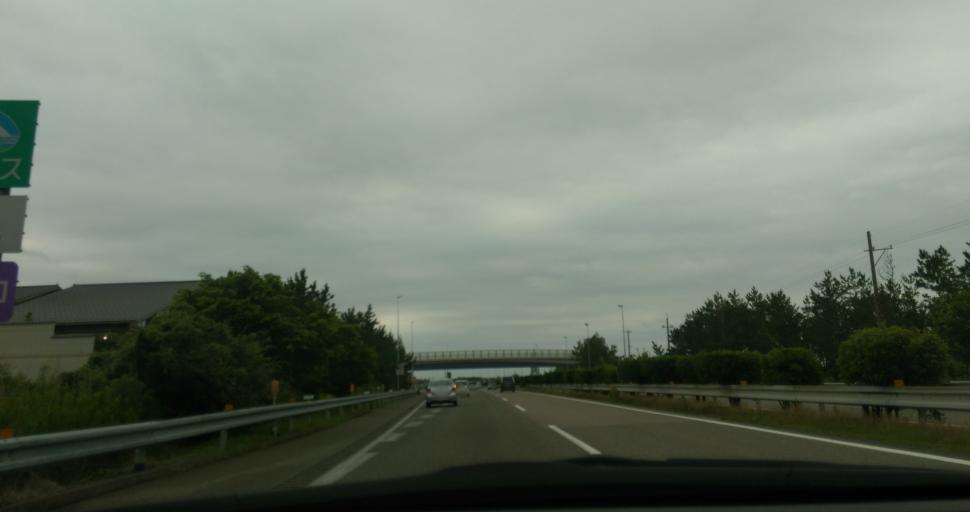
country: JP
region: Ishikawa
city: Matsuto
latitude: 36.5371
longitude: 136.5308
